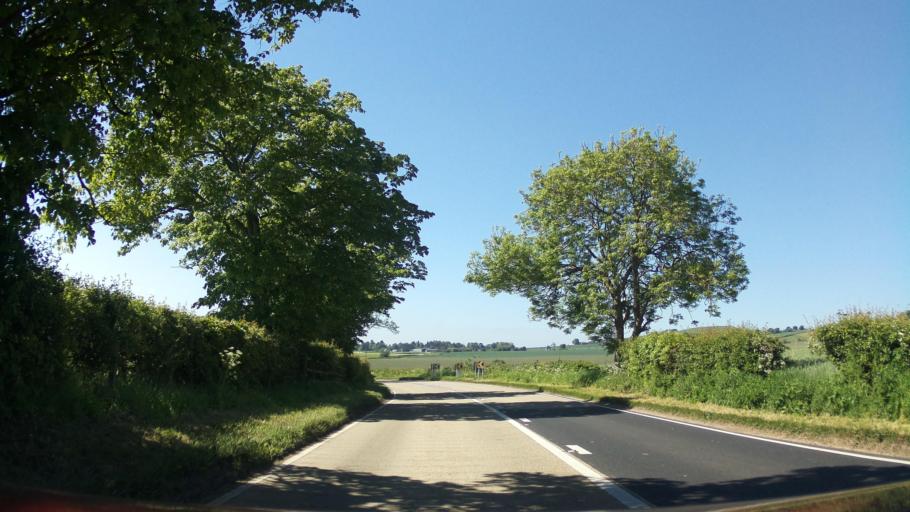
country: GB
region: Scotland
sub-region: Fife
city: Balmullo
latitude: 56.3716
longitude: -2.9311
